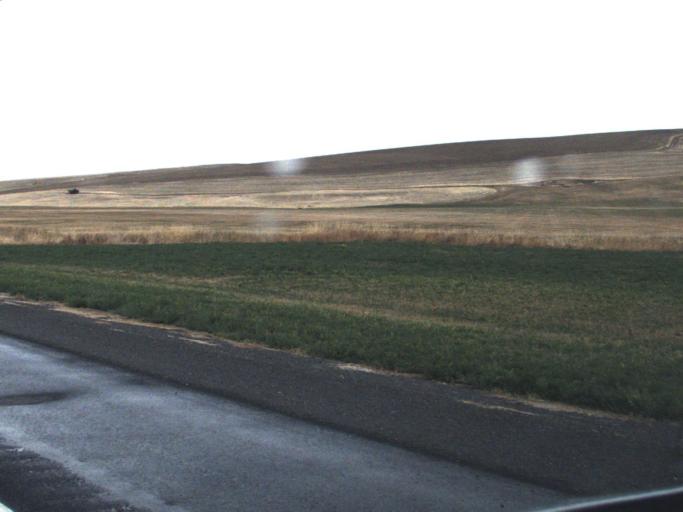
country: US
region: Washington
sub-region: Asotin County
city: Clarkston
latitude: 46.5634
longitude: -117.1116
